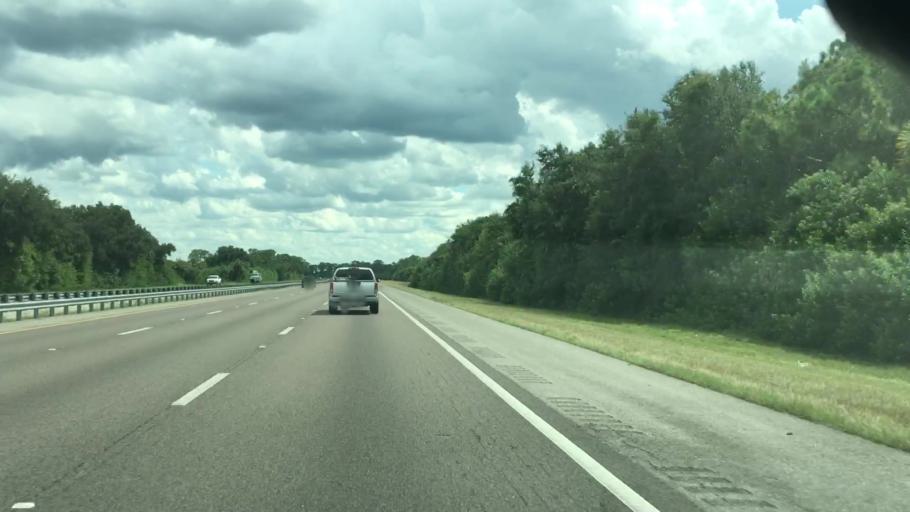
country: US
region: Florida
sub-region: Brevard County
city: Port Saint John
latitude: 28.5253
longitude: -80.8524
